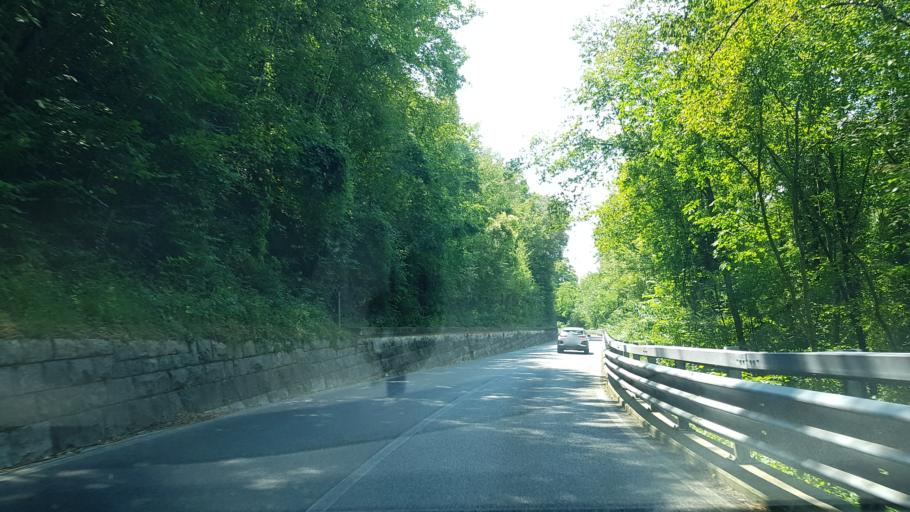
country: IT
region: Friuli Venezia Giulia
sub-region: Provincia di Udine
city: Tarcento
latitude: 46.2258
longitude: 13.2255
